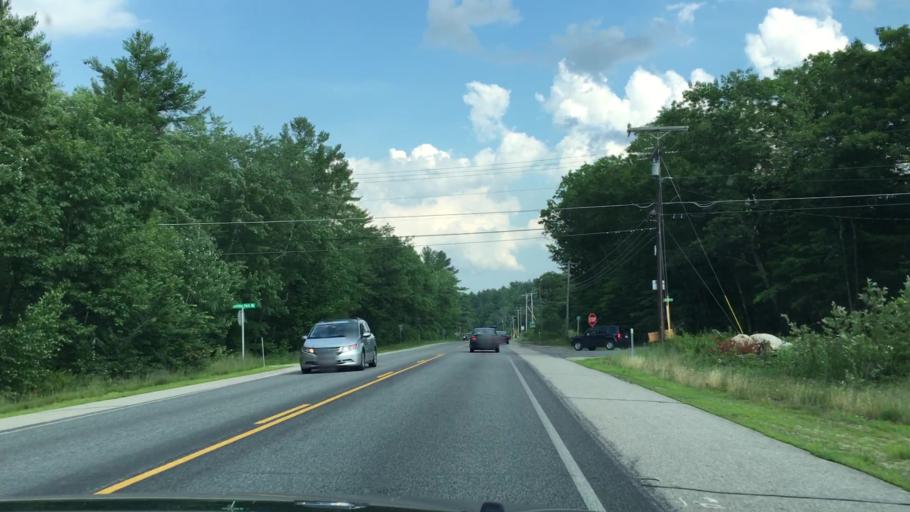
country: US
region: New Hampshire
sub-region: Strafford County
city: Farmington
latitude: 43.3890
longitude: -71.0861
